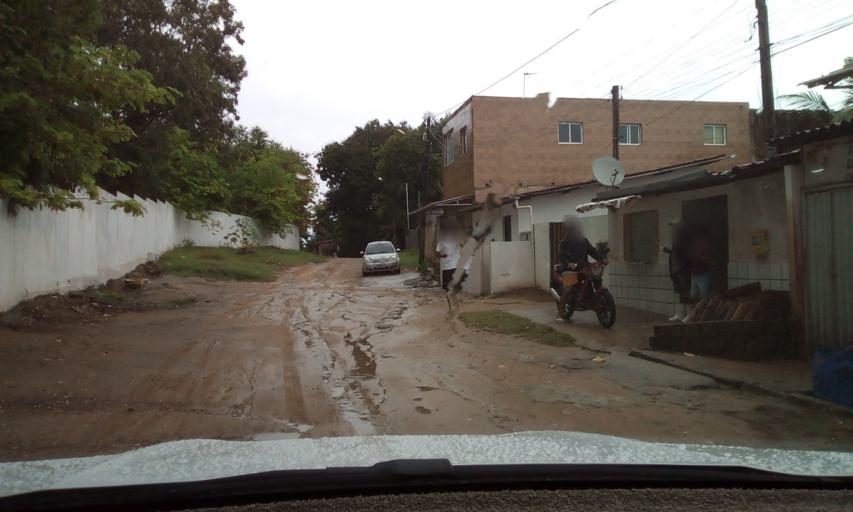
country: BR
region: Paraiba
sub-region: Joao Pessoa
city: Joao Pessoa
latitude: -7.1897
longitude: -34.8369
